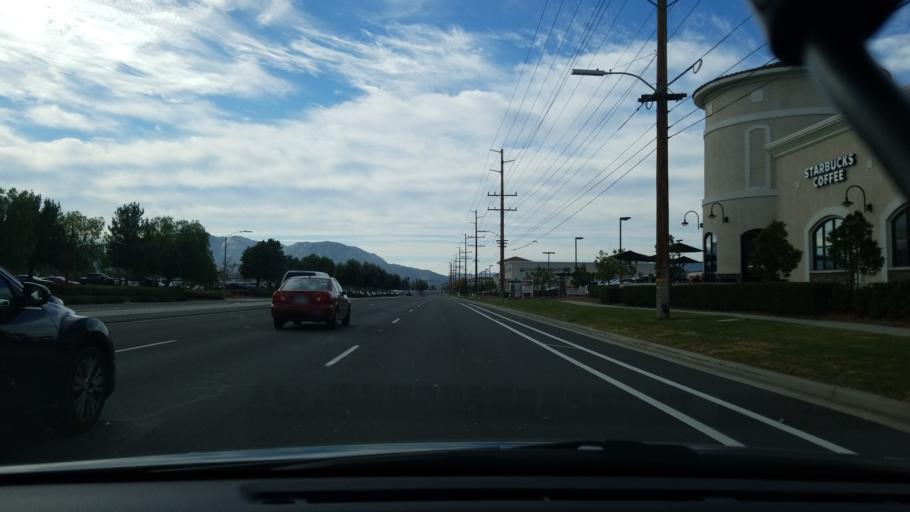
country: US
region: California
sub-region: Riverside County
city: Temecula
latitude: 33.4822
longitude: -117.0945
